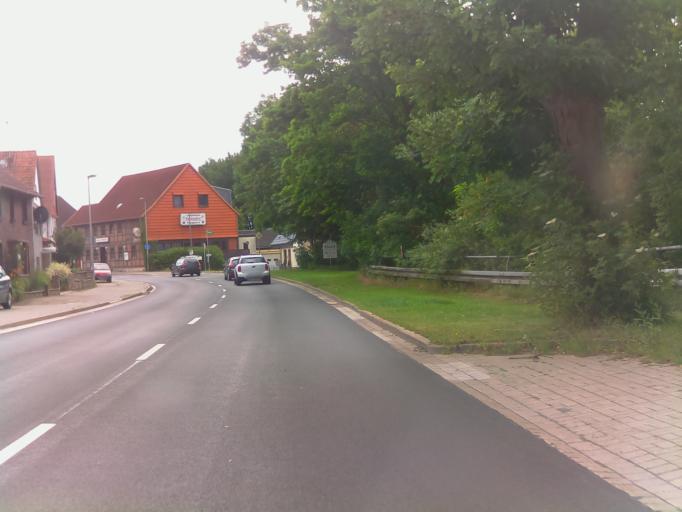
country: DE
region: Lower Saxony
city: Nordstemmen
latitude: 52.1460
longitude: 9.7694
